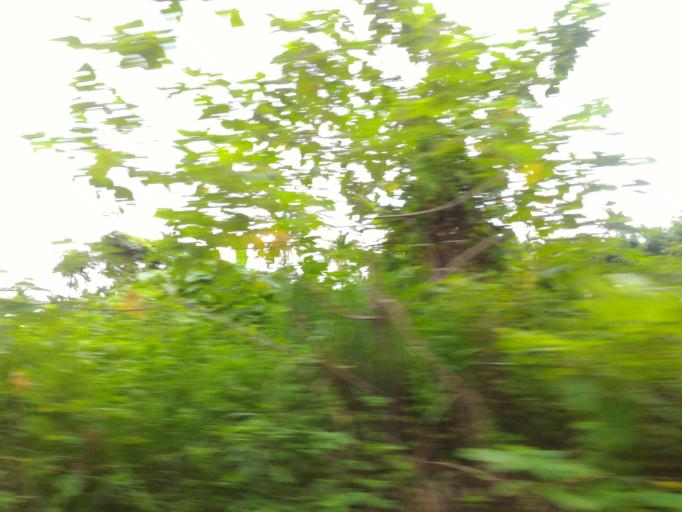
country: TW
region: Taipei
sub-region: Taipei
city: Banqiao
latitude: 25.0931
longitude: 121.4658
